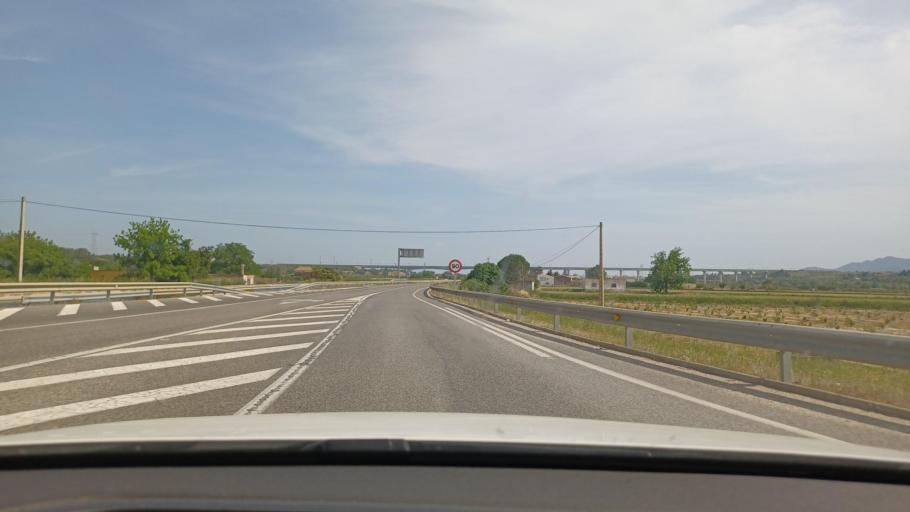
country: ES
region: Catalonia
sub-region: Provincia de Tarragona
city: Amposta
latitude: 40.7414
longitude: 0.5638
